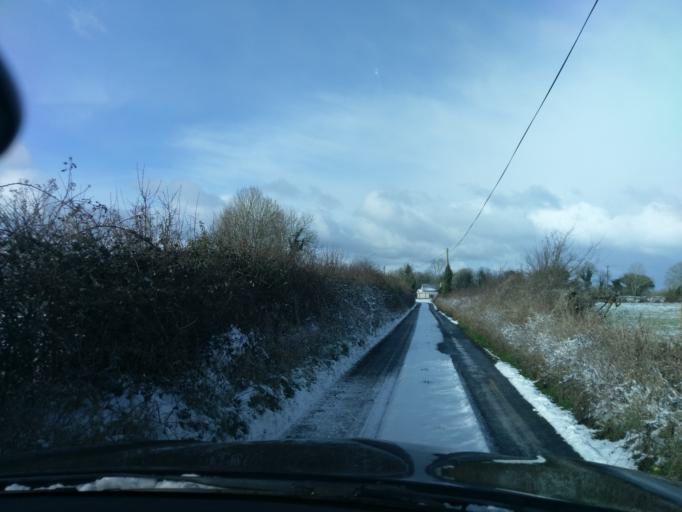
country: IE
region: Connaught
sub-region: County Galway
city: Athenry
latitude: 53.2159
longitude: -8.7626
